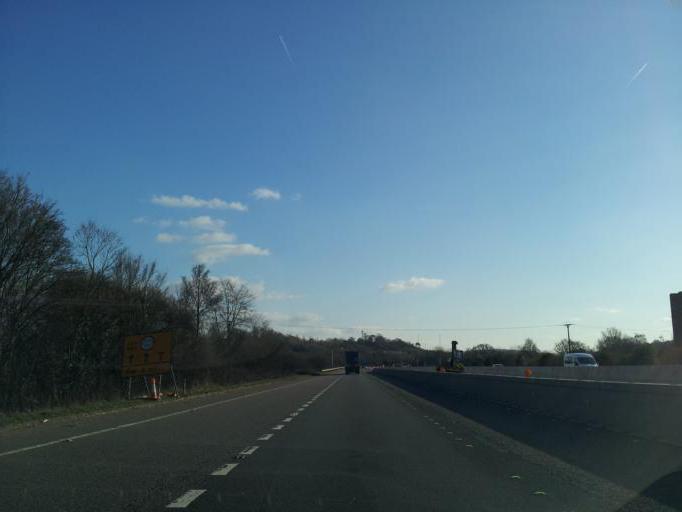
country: GB
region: England
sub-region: Devon
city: Cullompton
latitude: 50.8567
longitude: -3.3842
